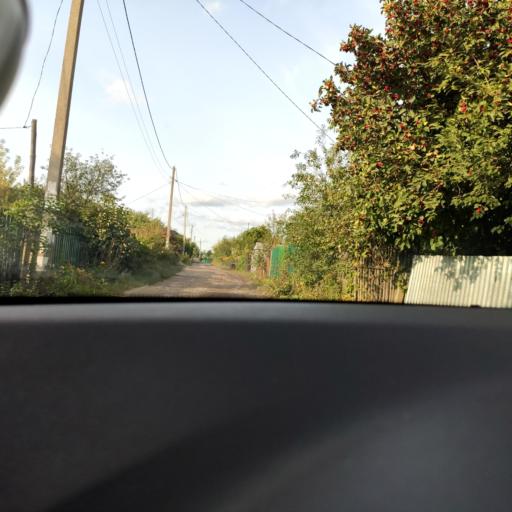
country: RU
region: Samara
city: Petra-Dubrava
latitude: 53.2854
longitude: 50.2947
